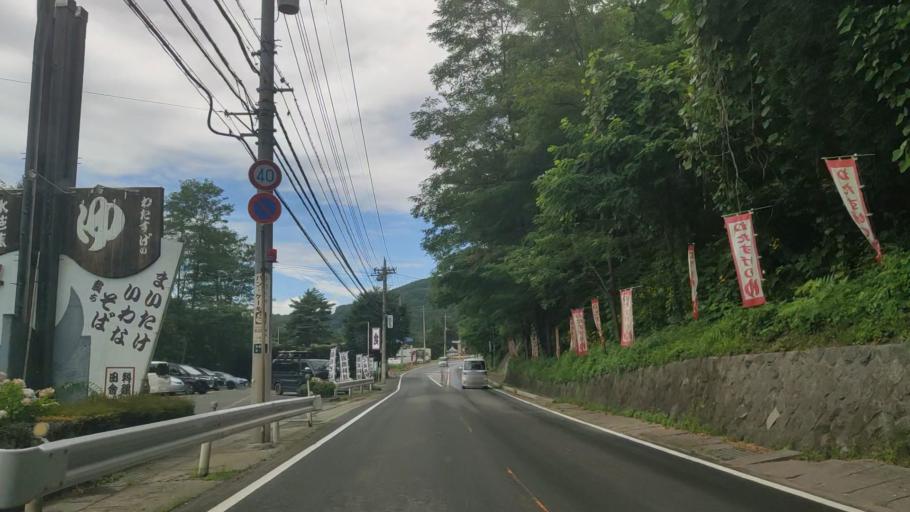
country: JP
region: Gunma
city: Numata
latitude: 36.7400
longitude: 139.2318
